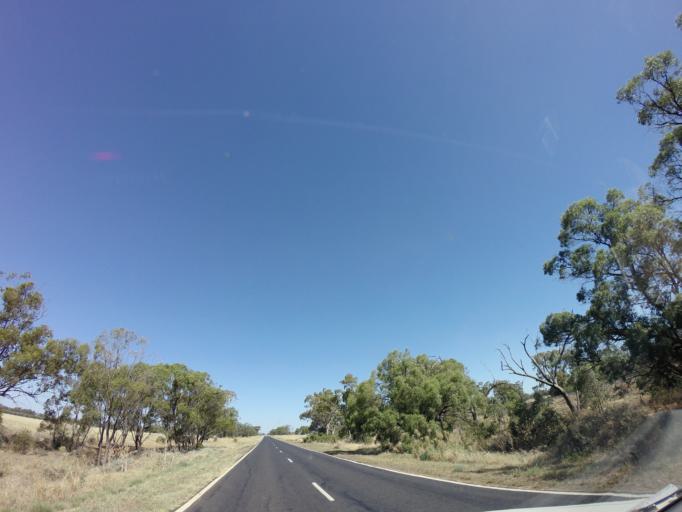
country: AU
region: New South Wales
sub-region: Bogan
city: Nyngan
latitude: -31.7711
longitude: 147.5909
